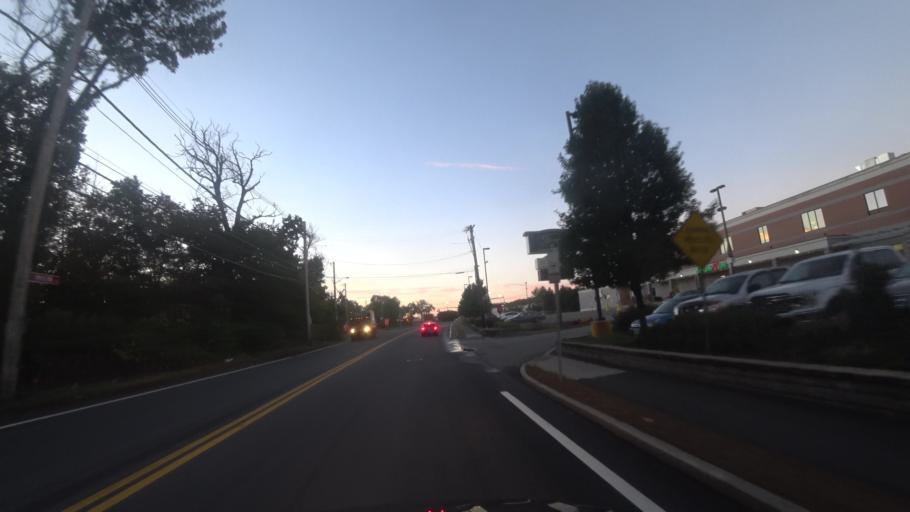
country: US
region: Massachusetts
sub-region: Essex County
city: Saugus
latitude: 42.4676
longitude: -71.0275
